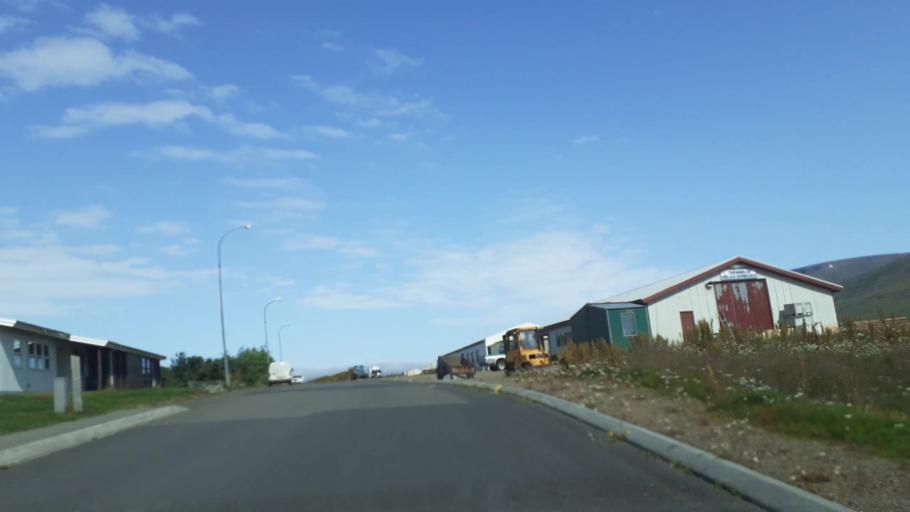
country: IS
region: Northwest
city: Saudarkrokur
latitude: 65.8275
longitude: -20.3164
